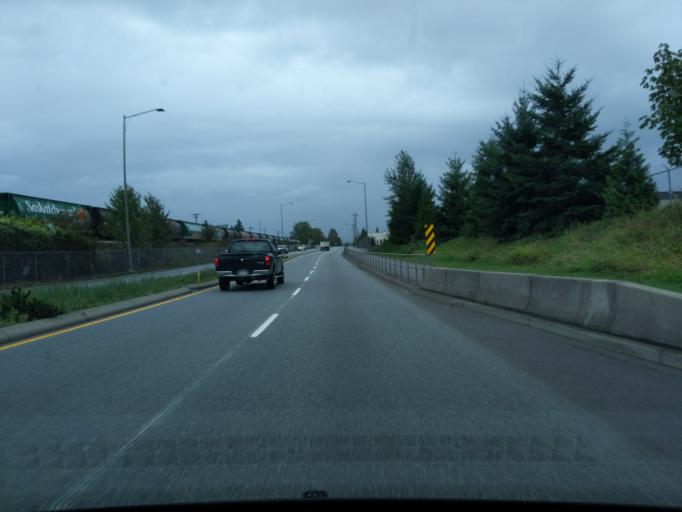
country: CA
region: British Columbia
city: Pitt Meadows
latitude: 49.1805
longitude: -122.7063
